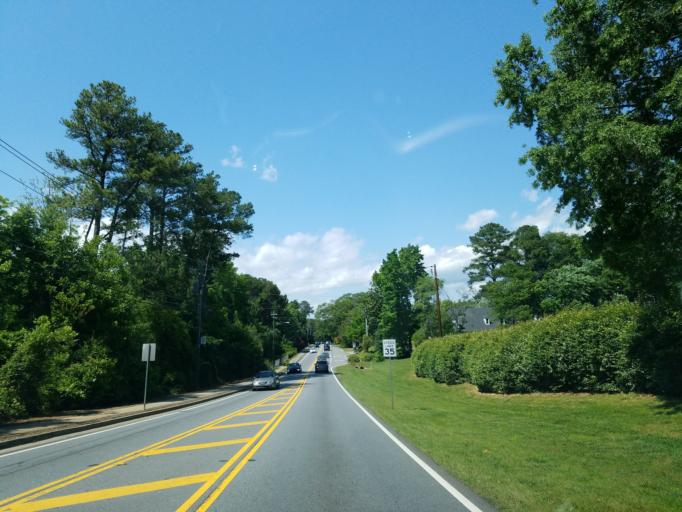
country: US
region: Georgia
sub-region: Fulton County
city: Roswell
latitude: 34.0474
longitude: -84.3436
